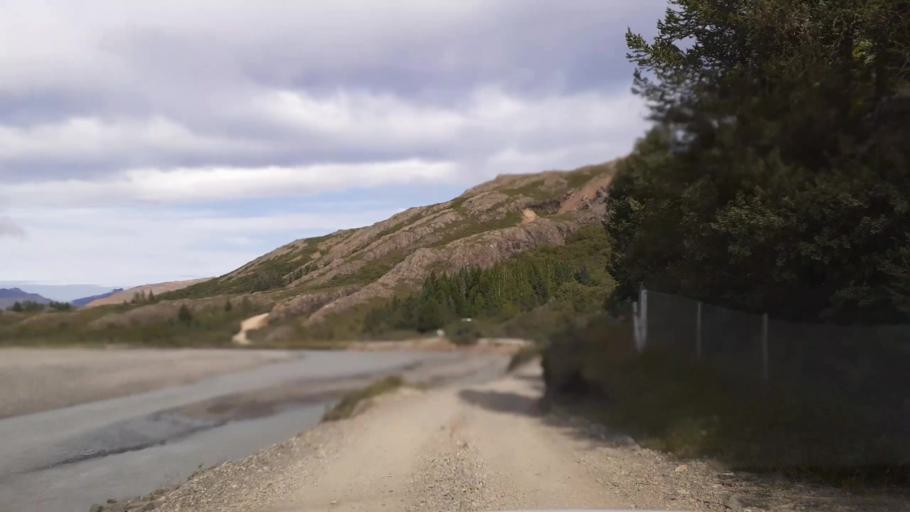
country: IS
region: East
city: Hoefn
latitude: 64.4362
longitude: -14.9077
